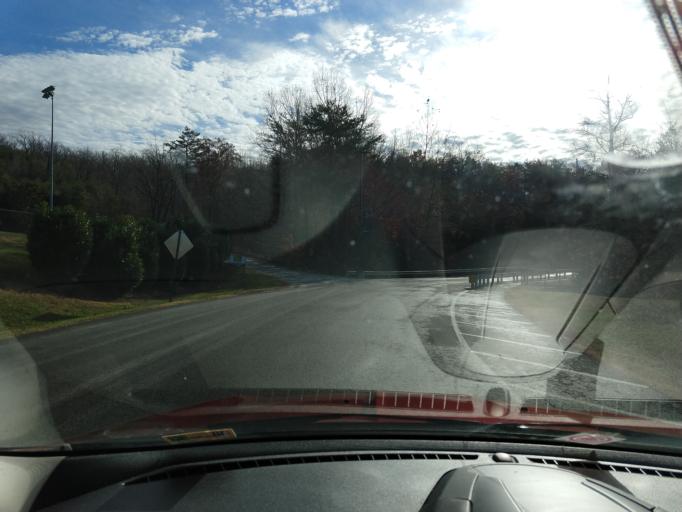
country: US
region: Virginia
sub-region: City of Lynchburg
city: West Lynchburg
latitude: 37.3430
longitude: -79.1824
